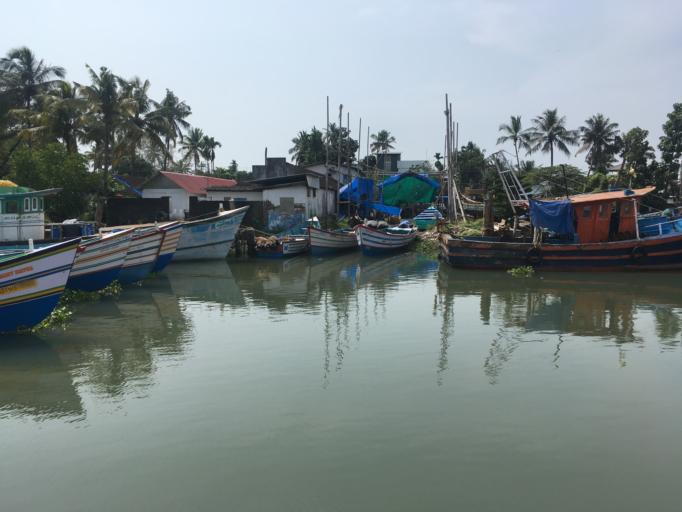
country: IN
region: Kerala
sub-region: Ernakulam
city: Cochin
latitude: 9.9786
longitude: 76.2419
